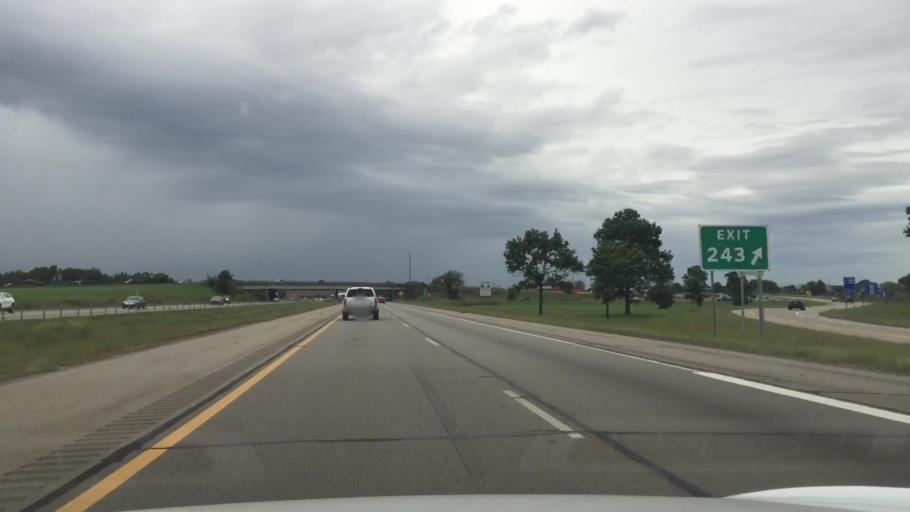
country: US
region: Michigan
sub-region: Macomb County
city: New Haven
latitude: 42.6767
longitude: -82.8172
